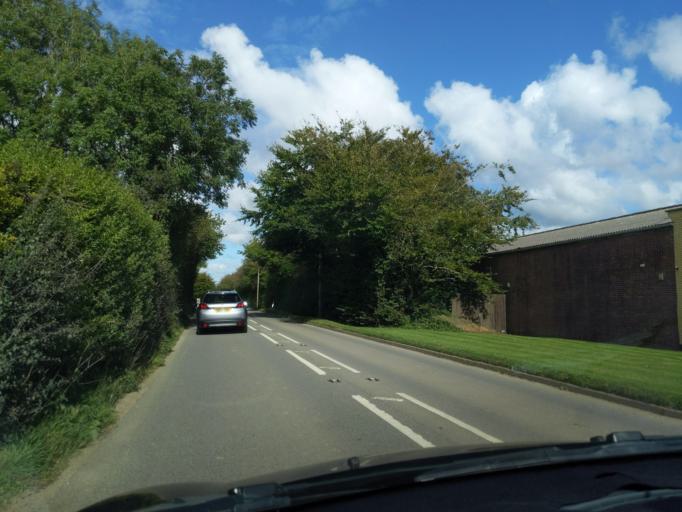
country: GB
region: England
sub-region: Devon
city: Holsworthy
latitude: 50.8512
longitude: -4.3330
